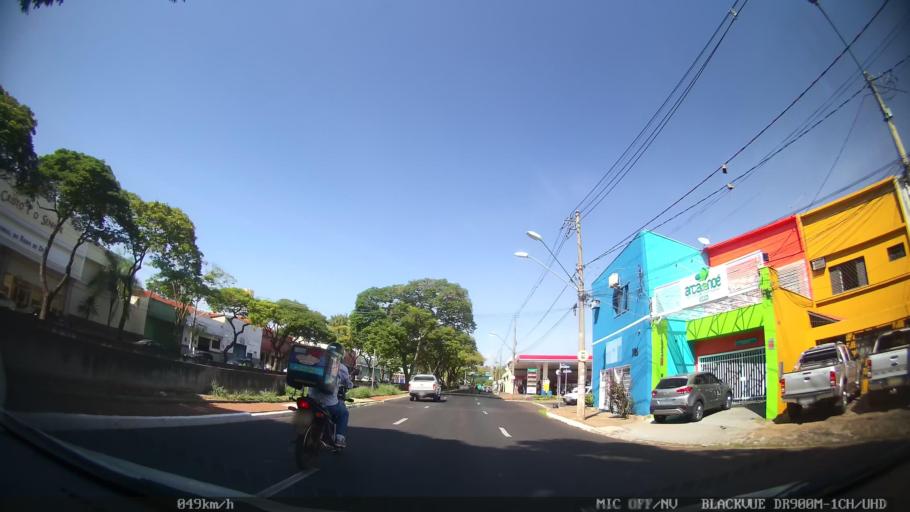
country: BR
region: Sao Paulo
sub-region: Ribeirao Preto
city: Ribeirao Preto
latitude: -21.1778
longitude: -47.8015
